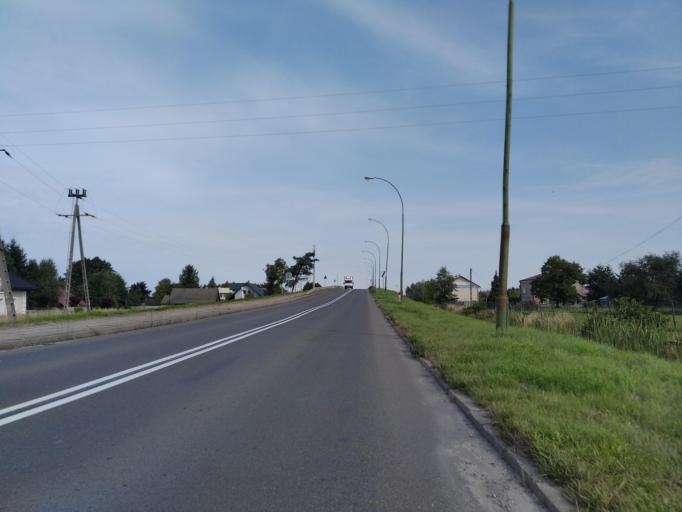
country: PL
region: Subcarpathian Voivodeship
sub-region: Powiat ropczycko-sedziszowski
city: Ostrow
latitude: 50.0765
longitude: 21.5838
